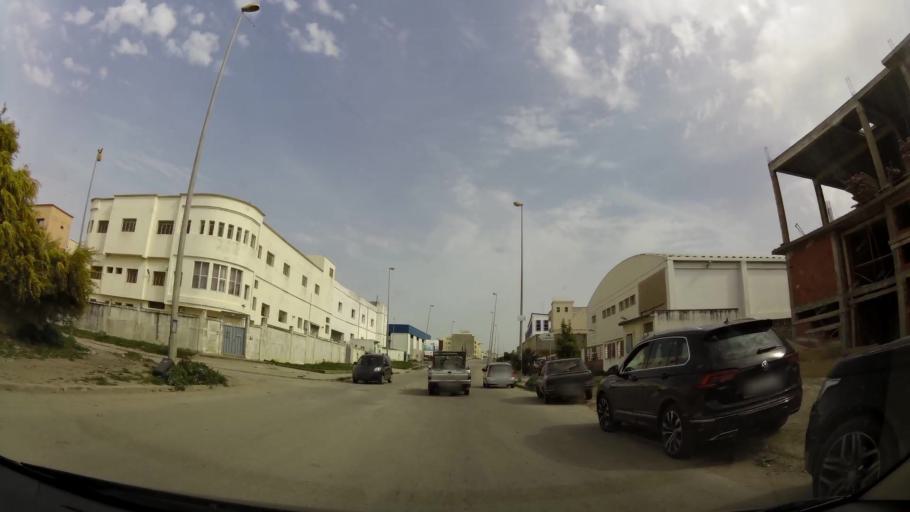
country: MA
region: Tanger-Tetouan
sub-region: Tanger-Assilah
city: Boukhalef
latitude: 35.7141
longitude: -5.8964
